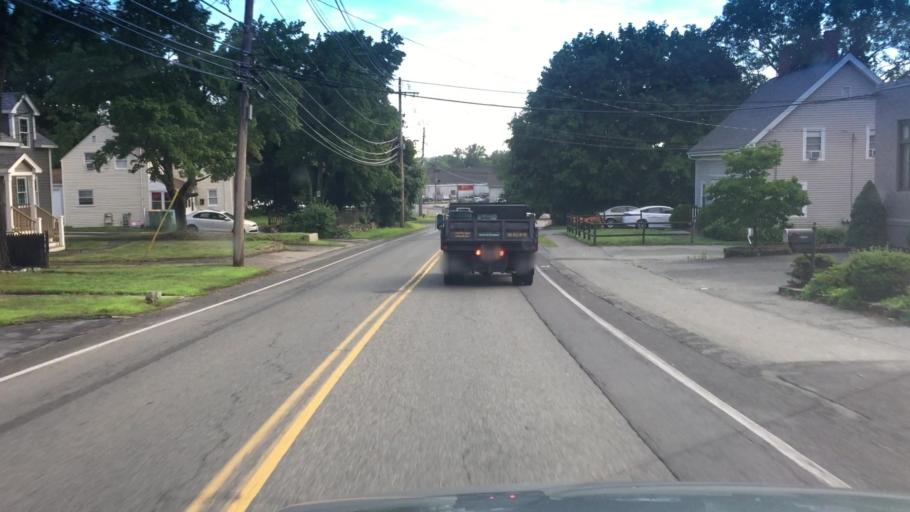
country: US
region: Massachusetts
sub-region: Norfolk County
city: Norwood
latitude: 42.1737
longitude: -71.2009
